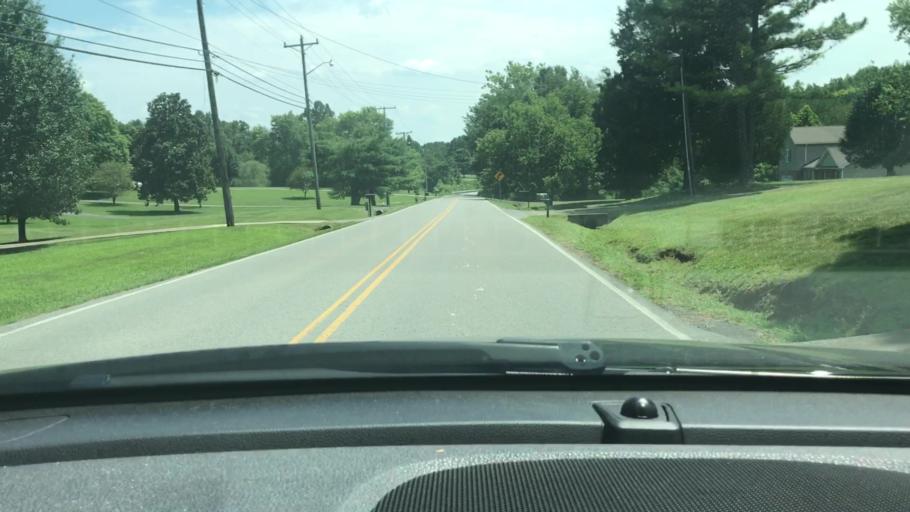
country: US
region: Tennessee
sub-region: Sumner County
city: White House
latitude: 36.4628
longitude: -86.6474
